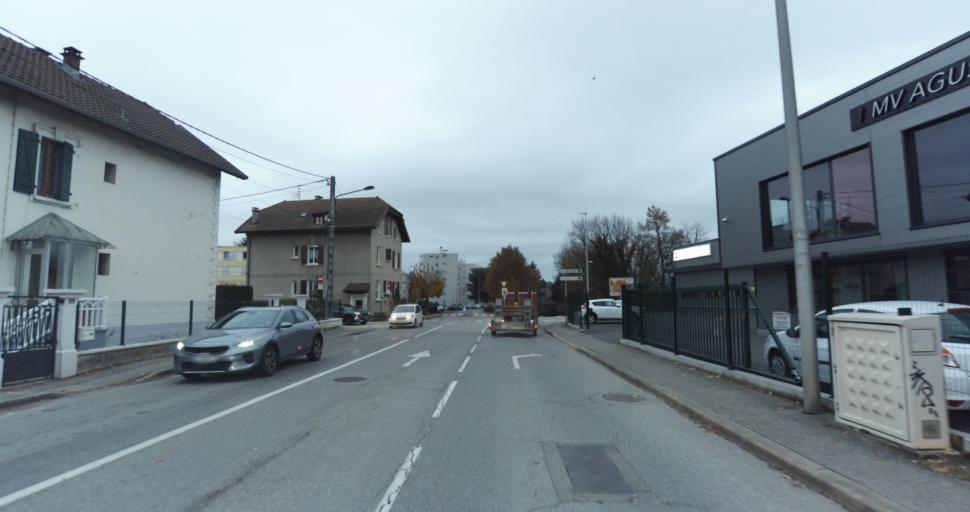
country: FR
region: Rhone-Alpes
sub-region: Departement de la Haute-Savoie
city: Annecy
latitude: 45.9124
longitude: 6.1123
